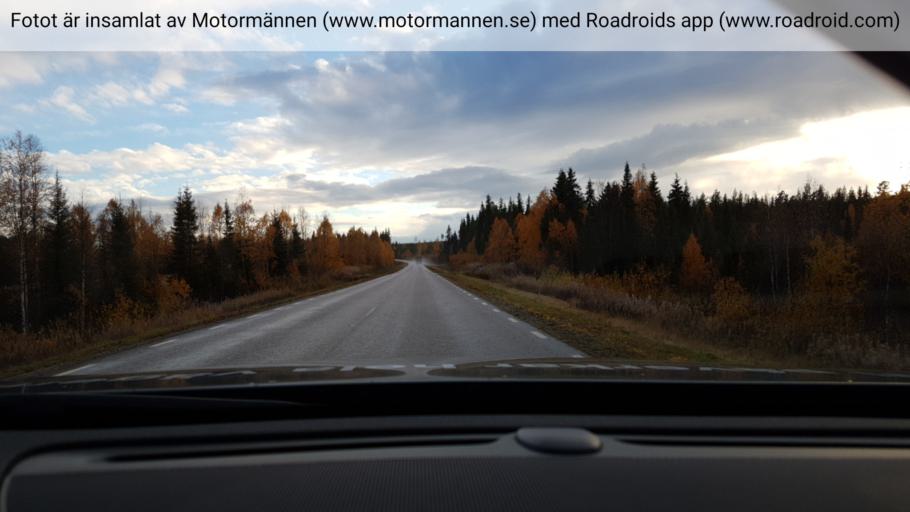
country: SE
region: Norrbotten
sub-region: Overkalix Kommun
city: OEverkalix
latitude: 66.7611
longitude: 22.6803
